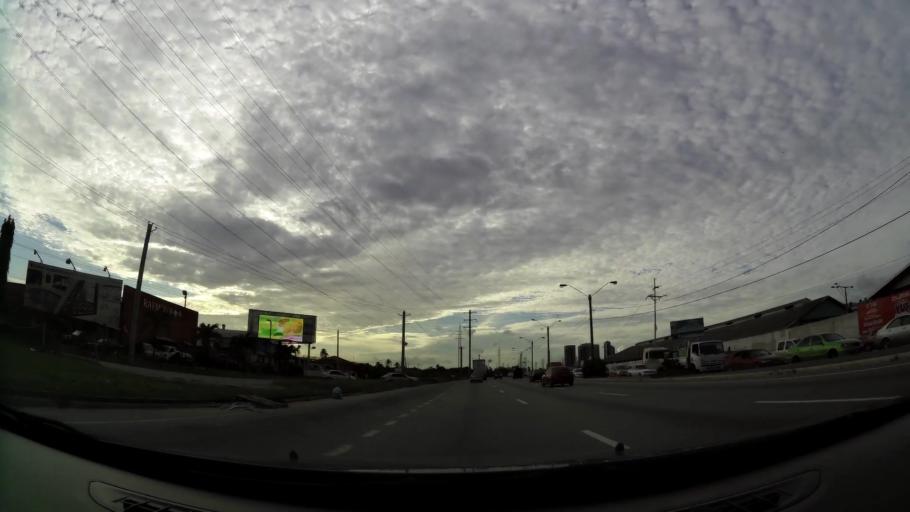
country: TT
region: San Juan/Laventille
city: Laventille
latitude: 10.6447
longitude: -61.4995
